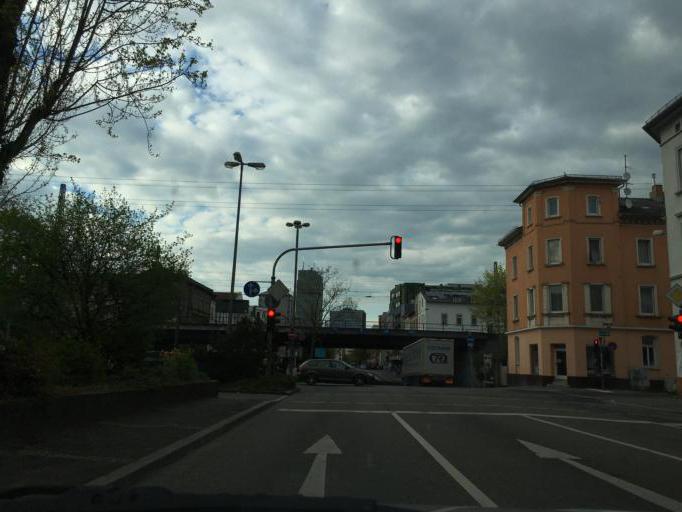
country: DE
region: Hesse
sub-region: Regierungsbezirk Darmstadt
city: Offenbach
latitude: 50.0993
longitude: 8.7661
